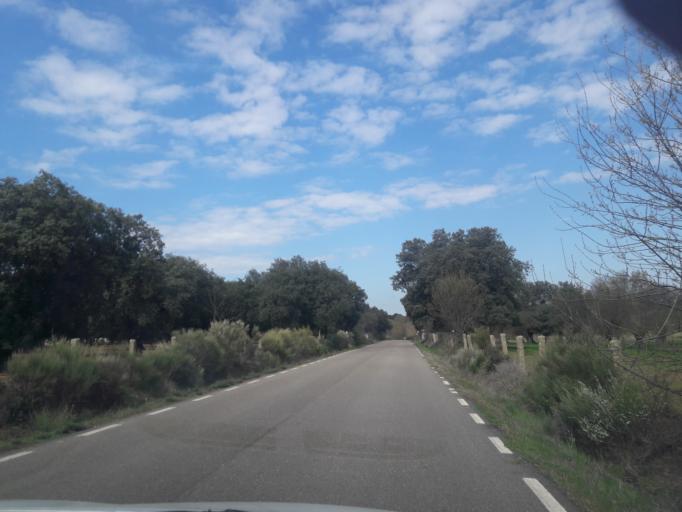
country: ES
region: Castille and Leon
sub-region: Provincia de Salamanca
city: Zamarra
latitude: 40.5556
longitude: -6.4496
